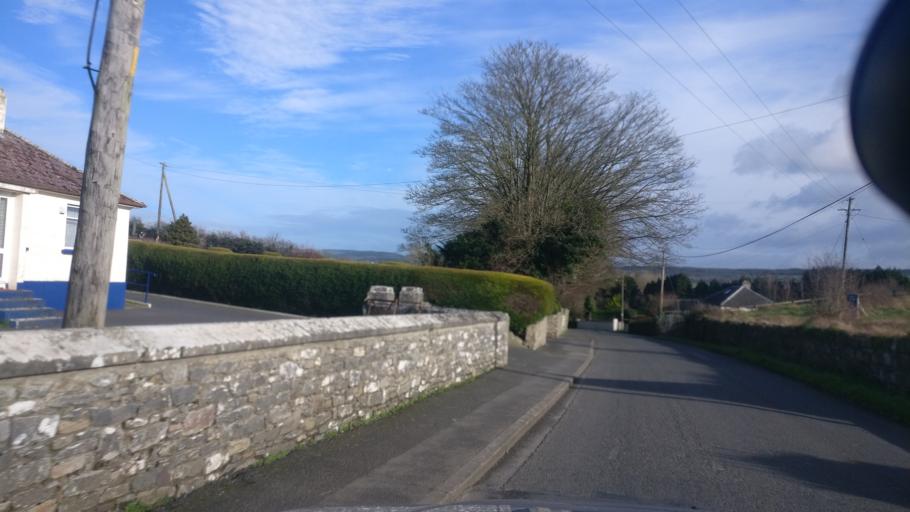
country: IE
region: Leinster
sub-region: Kilkenny
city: Thomastown
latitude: 52.5223
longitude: -7.1488
